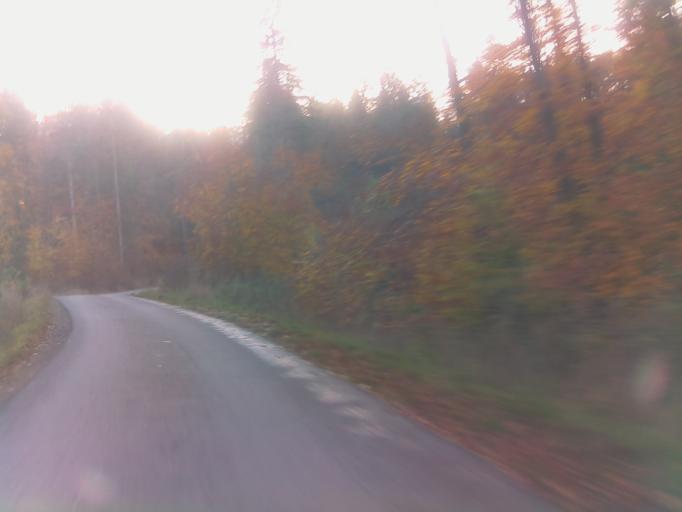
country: DE
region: Thuringia
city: Urnshausen
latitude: 50.7410
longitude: 10.1998
